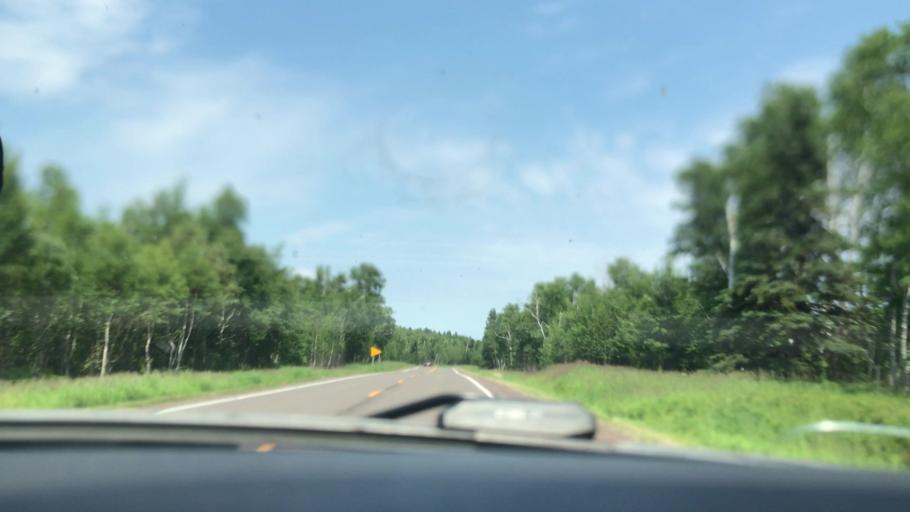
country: US
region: Minnesota
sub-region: Lake County
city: Silver Bay
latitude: 47.4905
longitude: -90.9825
